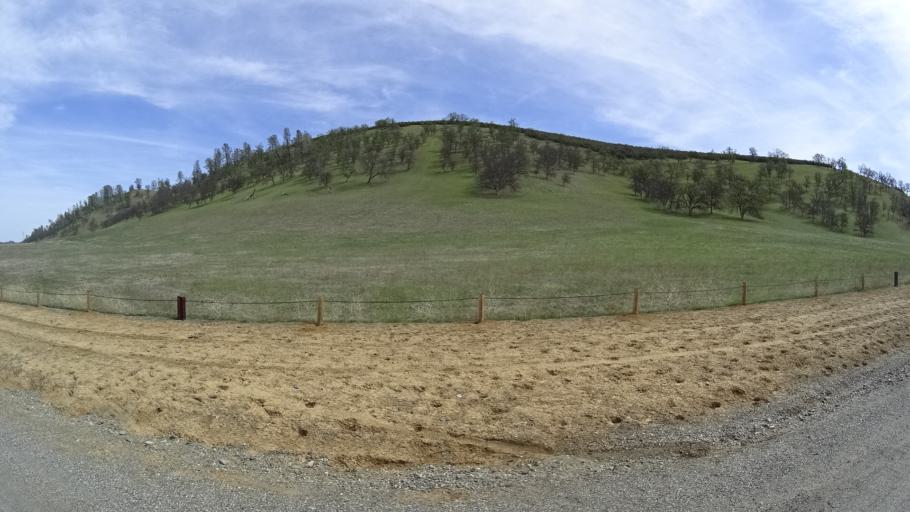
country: US
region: California
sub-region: Glenn County
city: Willows
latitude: 39.5931
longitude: -122.5247
